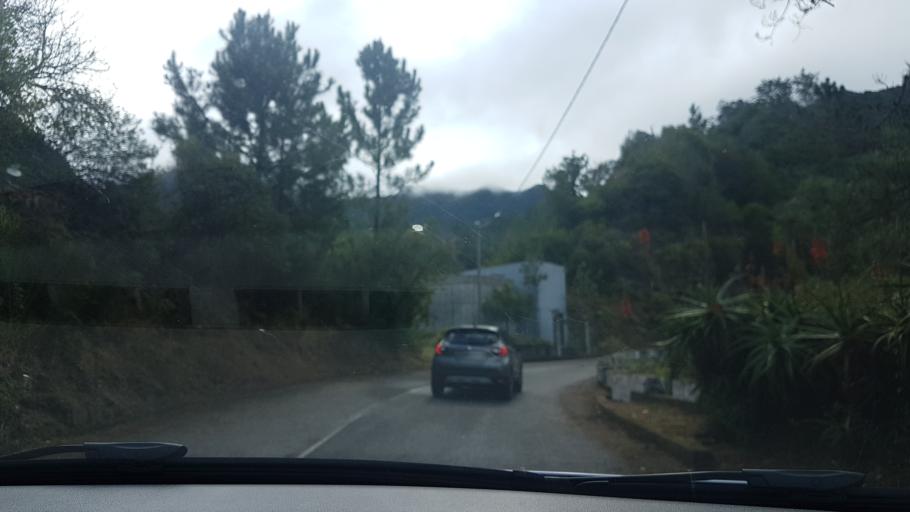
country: PT
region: Madeira
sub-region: Sao Vicente
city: Sao Vicente
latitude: 32.7728
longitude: -17.0268
